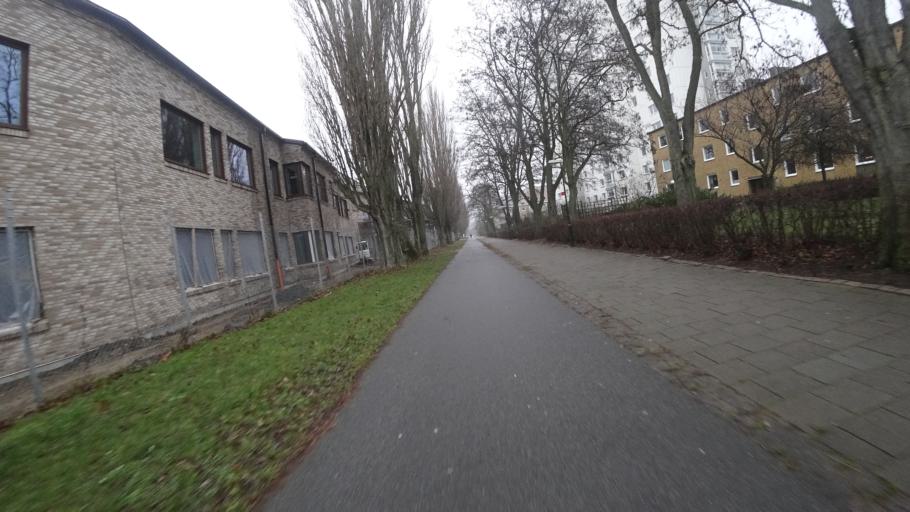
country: SE
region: Skane
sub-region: Malmo
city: Malmoe
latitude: 55.5835
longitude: 12.9947
